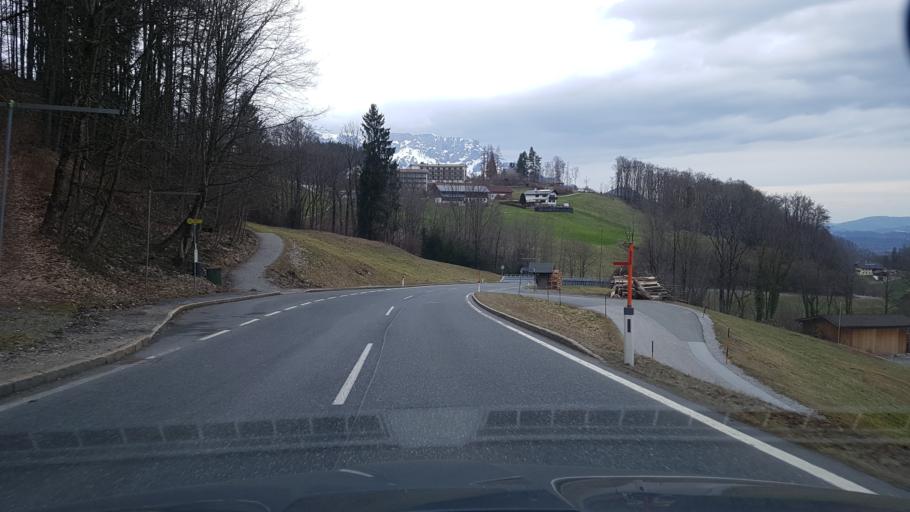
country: AT
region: Salzburg
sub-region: Politischer Bezirk Hallein
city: Hallein
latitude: 47.6617
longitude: 13.0954
